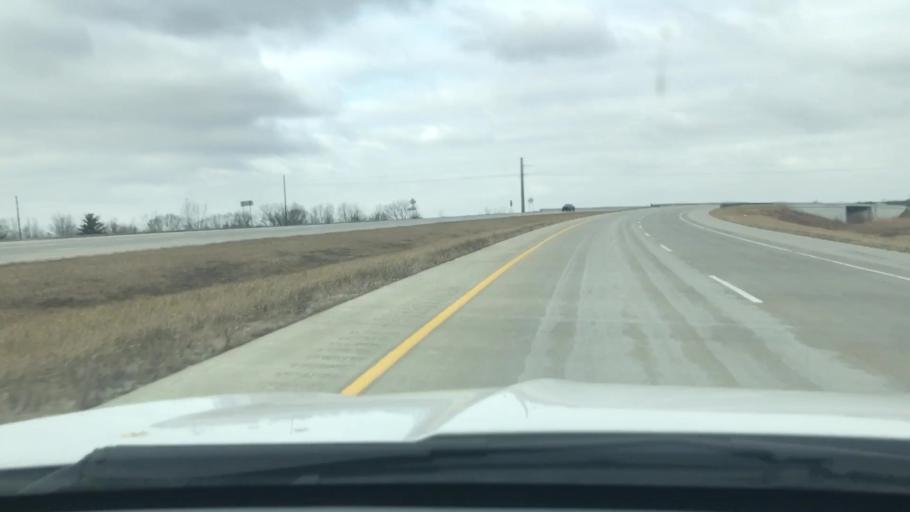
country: US
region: Indiana
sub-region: Carroll County
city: Delphi
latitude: 40.5958
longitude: -86.6552
